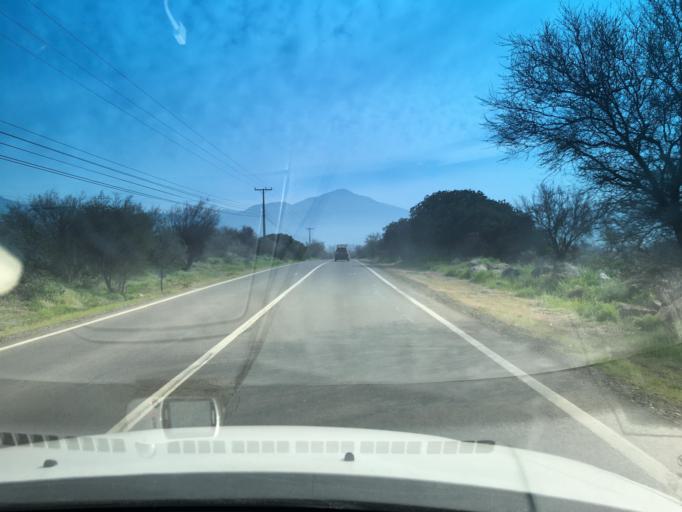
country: CL
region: Santiago Metropolitan
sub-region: Provincia de Chacabuco
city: Lampa
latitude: -33.1332
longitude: -70.9213
